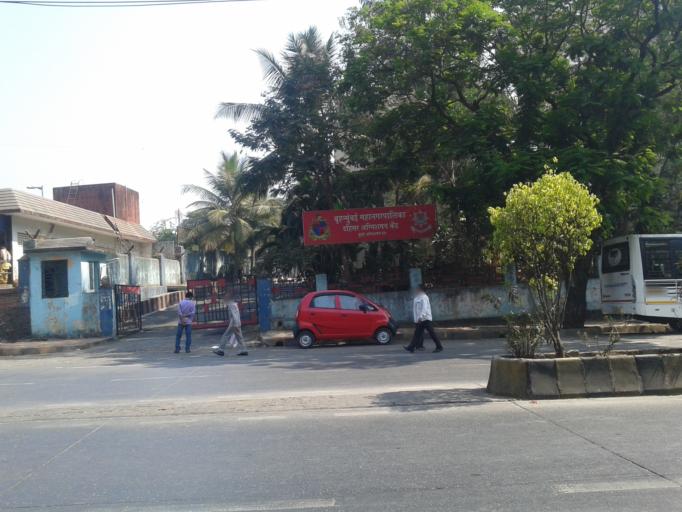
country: IN
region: Maharashtra
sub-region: Mumbai Suburban
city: Borivli
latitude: 19.2479
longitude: 72.8621
